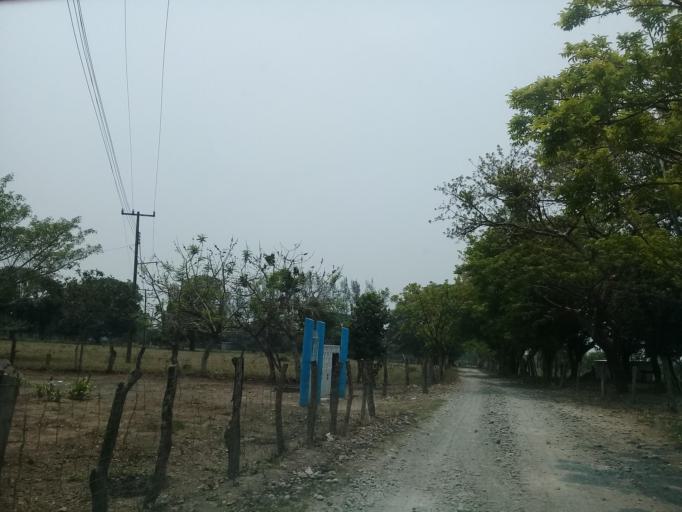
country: MX
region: Veracruz
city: Jamapa
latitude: 18.9323
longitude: -96.2129
